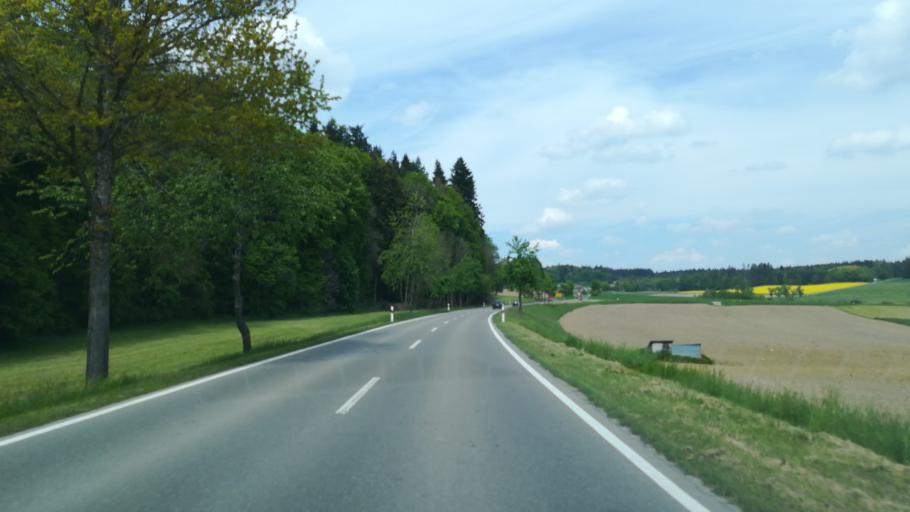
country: DE
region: Baden-Wuerttemberg
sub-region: Freiburg Region
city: Stockach
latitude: 47.8793
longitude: 9.0373
